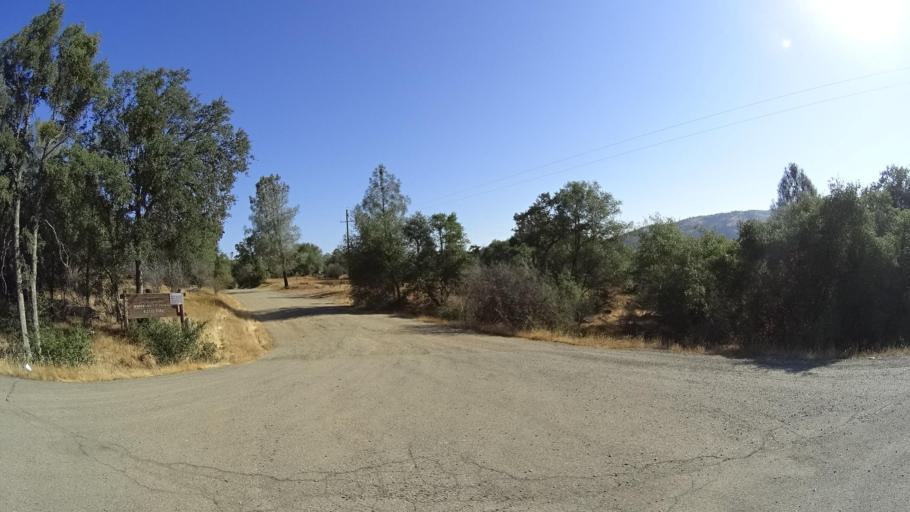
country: US
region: California
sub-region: Mariposa County
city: Mariposa
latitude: 37.5689
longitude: -120.1416
